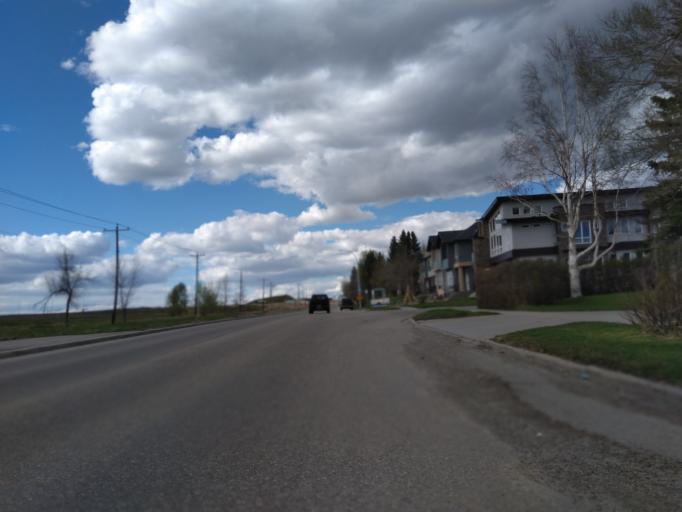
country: CA
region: Alberta
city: Calgary
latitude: 51.0006
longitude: -114.1410
